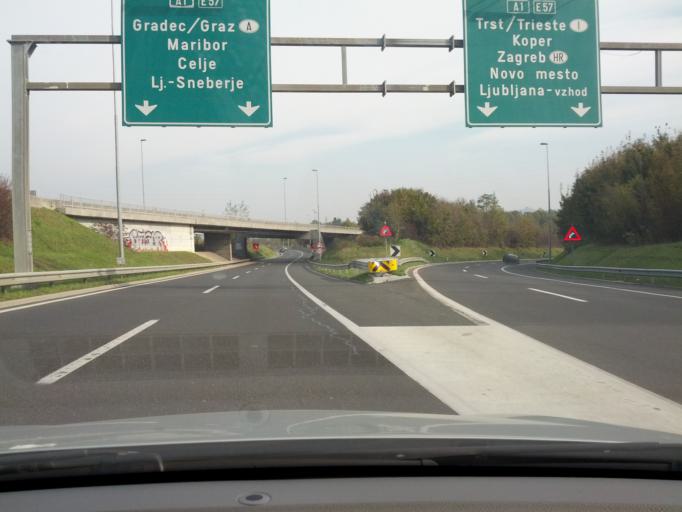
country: SI
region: Dol pri Ljubljani
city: Dol pri Ljubljani
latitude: 46.0677
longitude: 14.5722
